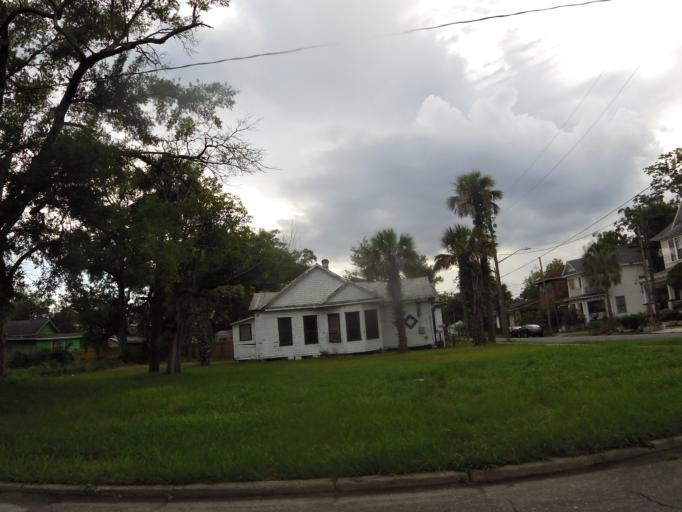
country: US
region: Florida
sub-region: Duval County
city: Jacksonville
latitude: 30.3421
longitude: -81.6740
